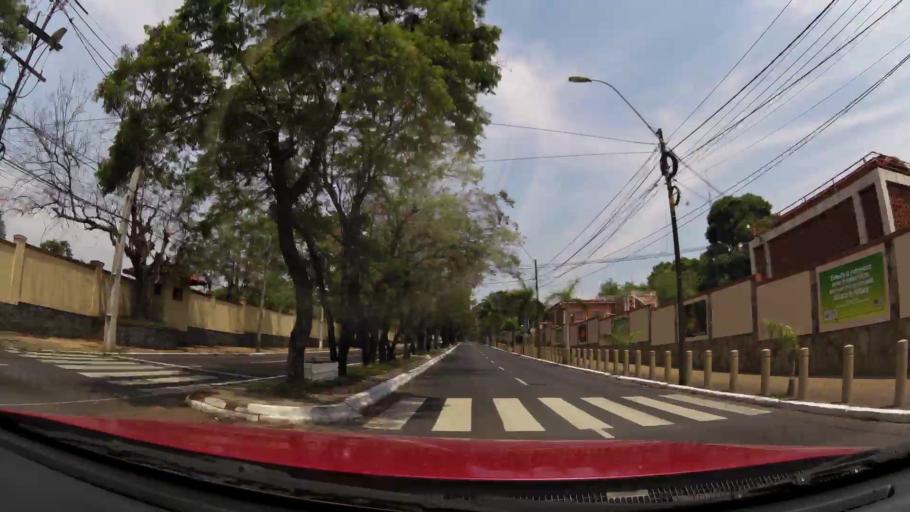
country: PY
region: Asuncion
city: Asuncion
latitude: -25.2936
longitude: -57.6035
